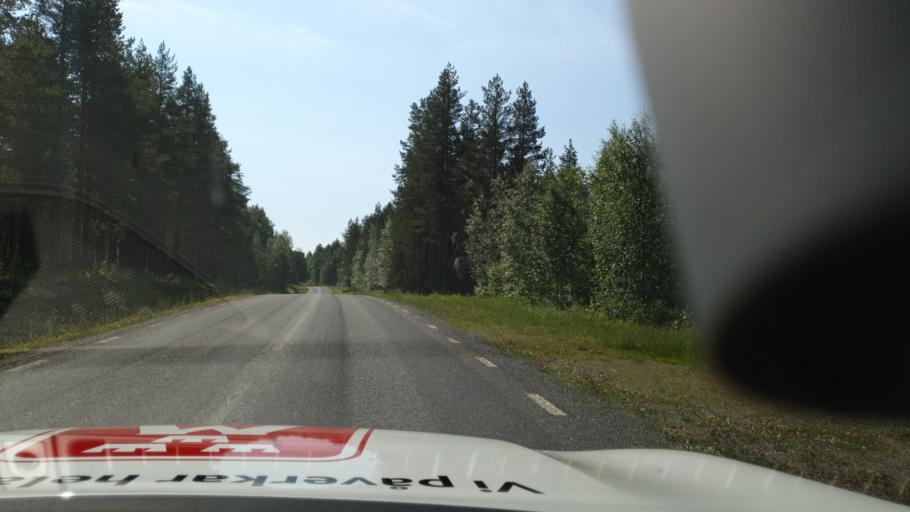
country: SE
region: Vaesterbotten
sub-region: Skelleftea Kommun
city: Langsele
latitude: 65.0182
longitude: 20.0764
